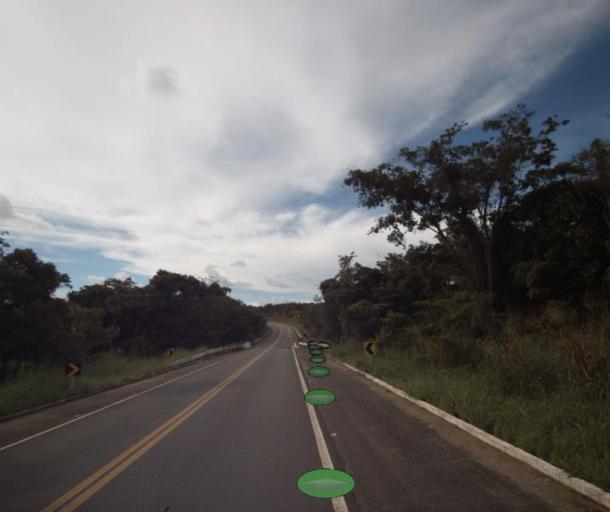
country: BR
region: Goias
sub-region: Barro Alto
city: Barro Alto
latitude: -15.1679
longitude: -48.7024
